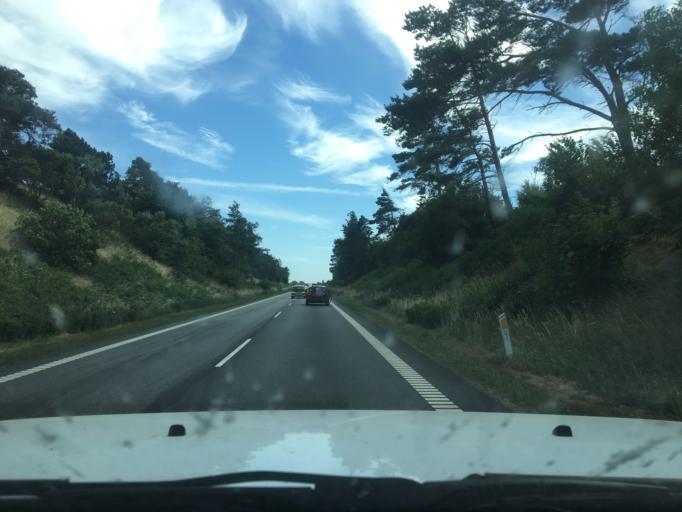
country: DK
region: Central Jutland
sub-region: Viborg Kommune
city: Viborg
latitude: 56.5630
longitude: 9.3857
